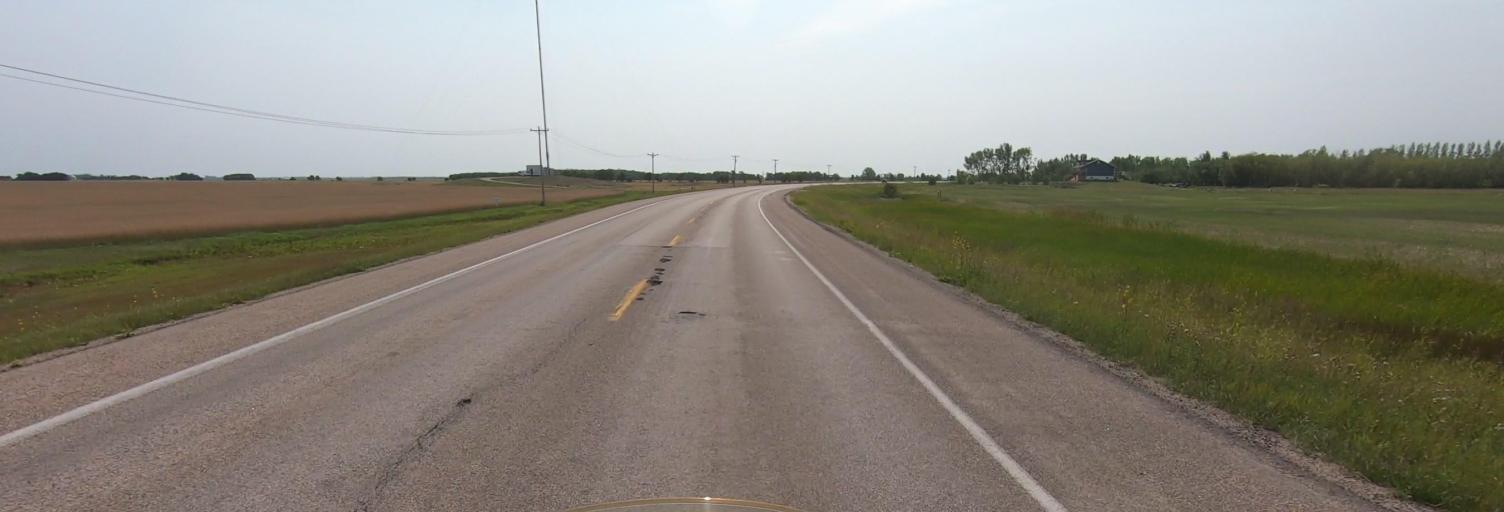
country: CA
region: Manitoba
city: Niverville
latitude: 49.6620
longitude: -97.1048
